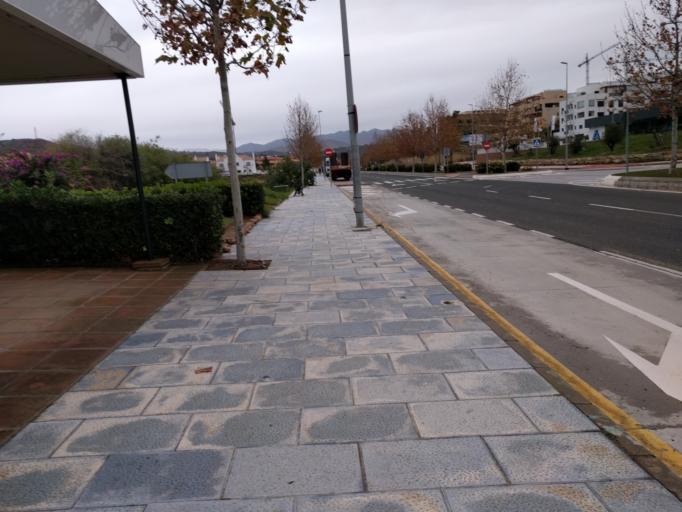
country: ES
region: Andalusia
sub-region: Provincia de Malaga
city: Fuengirola
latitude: 36.5064
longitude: -4.6826
